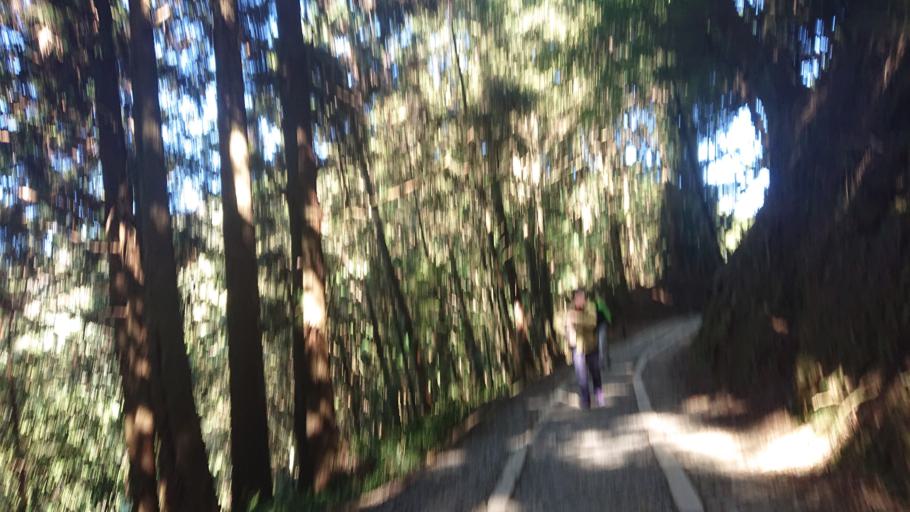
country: TW
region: Taiwan
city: Lugu
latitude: 23.4821
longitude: 120.8249
